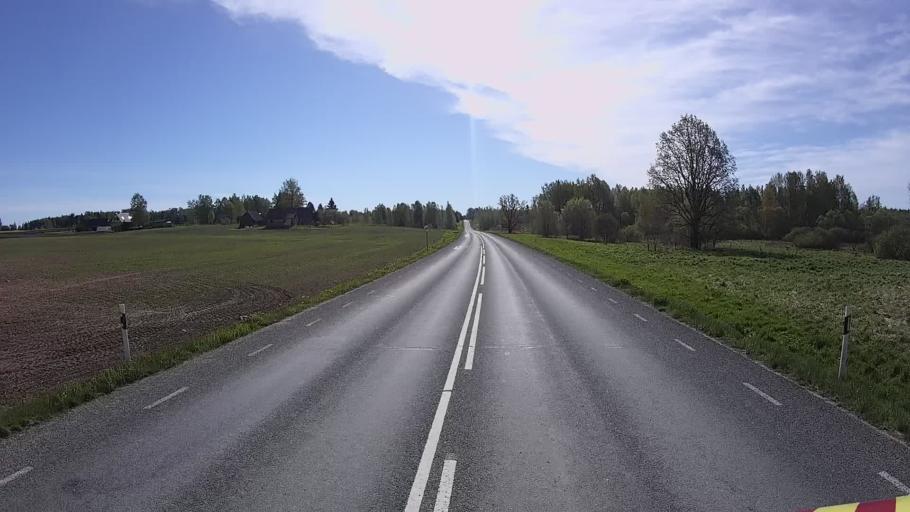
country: EE
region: Polvamaa
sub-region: Polva linn
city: Polva
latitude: 58.1589
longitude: 27.1670
